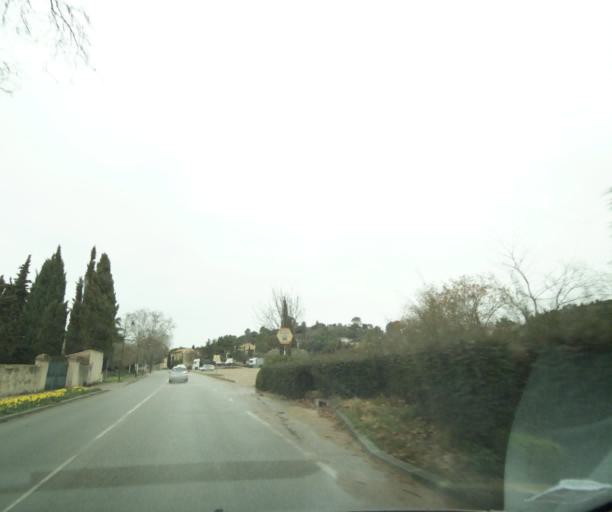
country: FR
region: Provence-Alpes-Cote d'Azur
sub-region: Departement des Bouches-du-Rhone
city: Rognes
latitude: 43.6598
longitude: 5.3537
